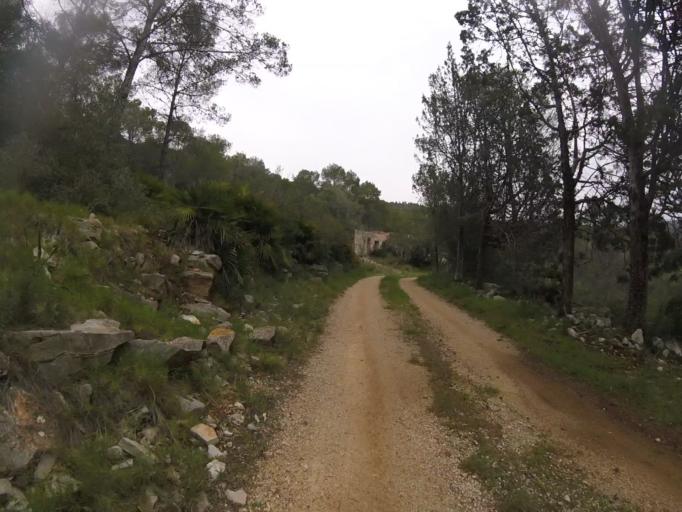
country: ES
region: Valencia
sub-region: Provincia de Castello
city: Santa Magdalena de Pulpis
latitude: 40.3195
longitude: 0.2811
